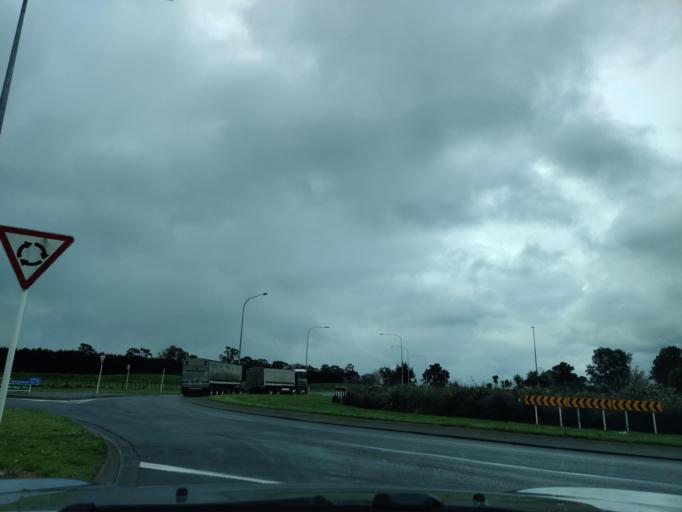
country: NZ
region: Hawke's Bay
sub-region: Hastings District
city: Hastings
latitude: -39.6588
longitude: 176.7944
